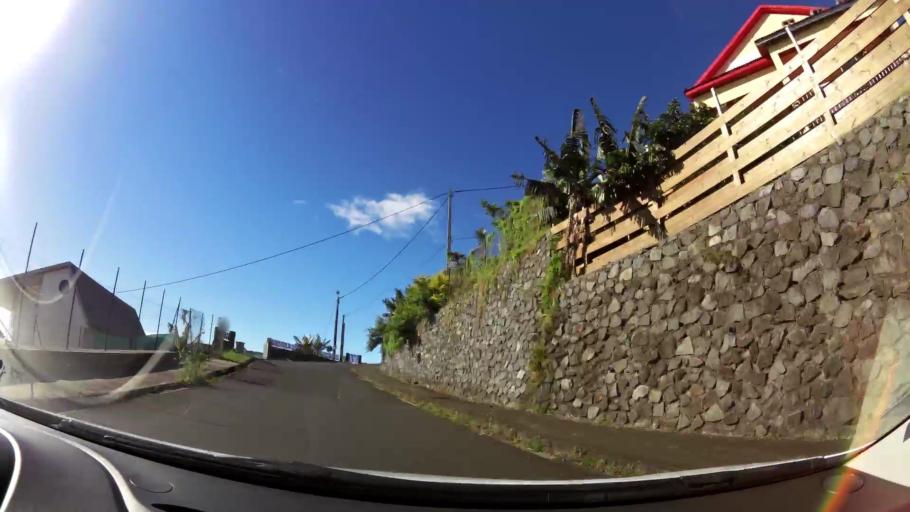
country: RE
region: Reunion
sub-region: Reunion
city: Saint-Denis
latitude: -20.9272
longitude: 55.4737
